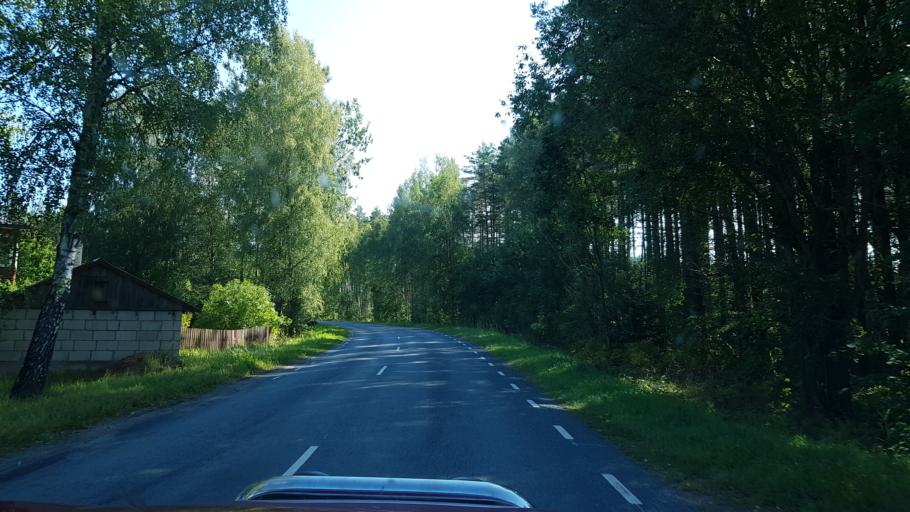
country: EE
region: Polvamaa
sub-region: Polva linn
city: Polva
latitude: 58.2678
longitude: 27.1369
